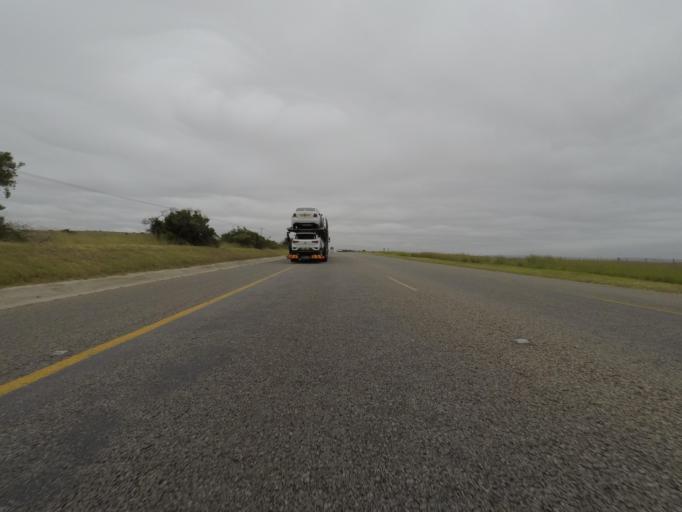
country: ZA
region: Eastern Cape
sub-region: Nelson Mandela Bay Metropolitan Municipality
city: Port Elizabeth
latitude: -33.6393
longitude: 25.8871
